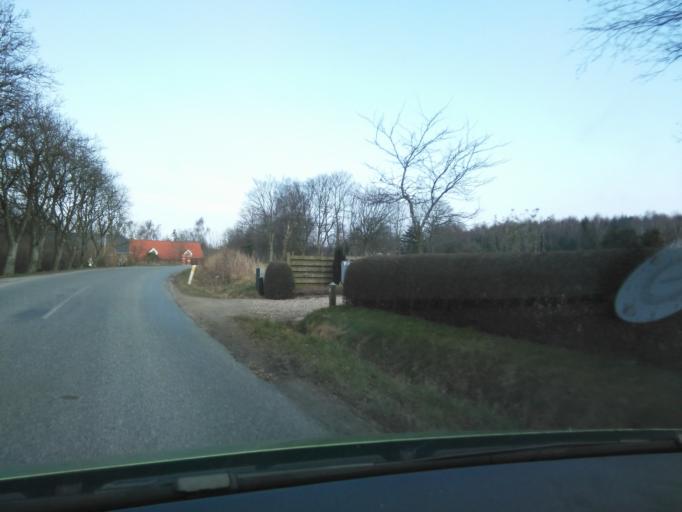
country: DK
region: Central Jutland
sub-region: Arhus Kommune
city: Beder
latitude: 56.0576
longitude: 10.2421
